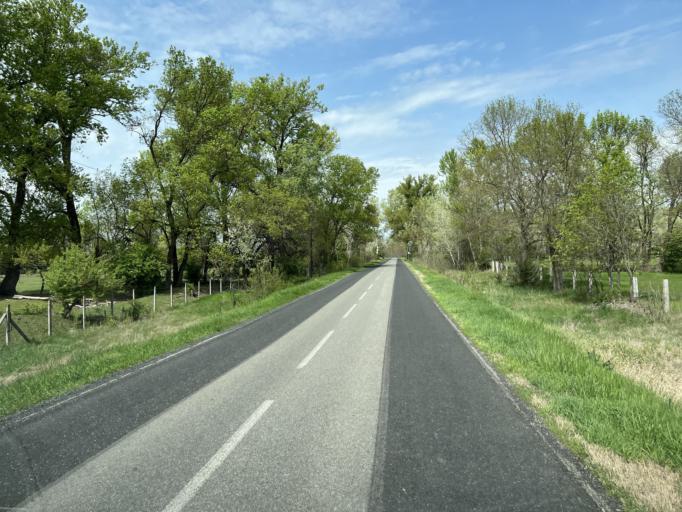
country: HU
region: Pest
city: Albertirsa
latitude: 47.1747
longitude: 19.6136
